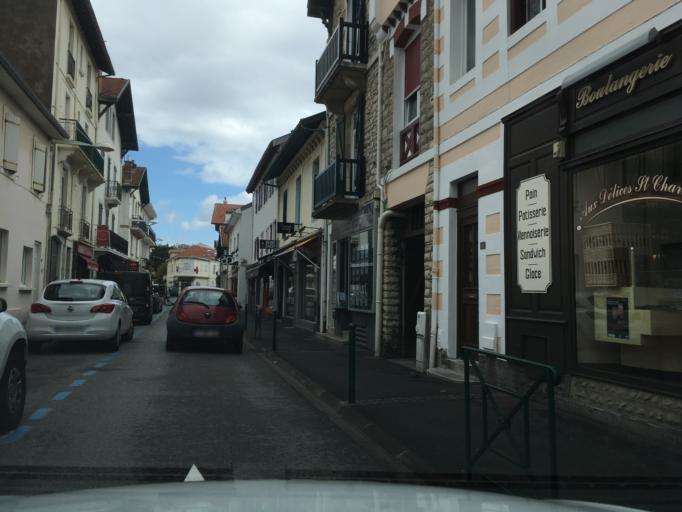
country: FR
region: Aquitaine
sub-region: Departement des Pyrenees-Atlantiques
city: Biarritz
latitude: 43.4860
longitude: -1.5515
